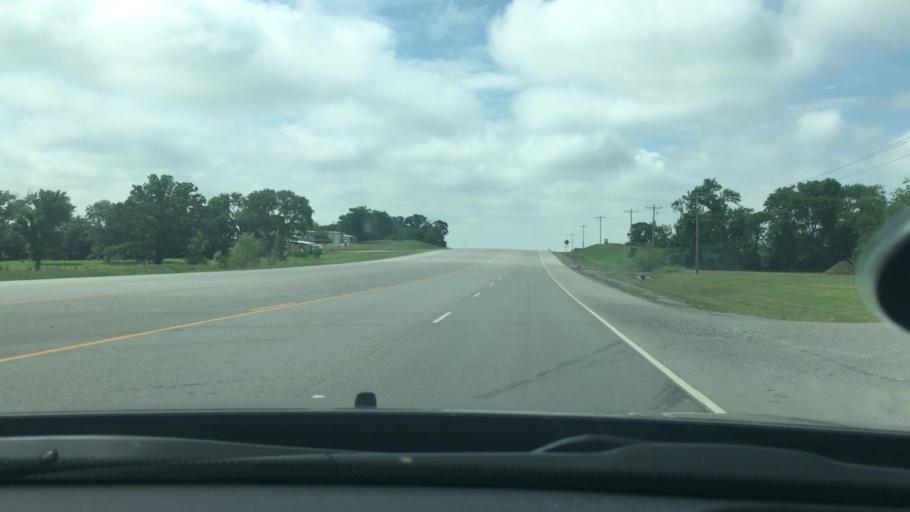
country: US
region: Oklahoma
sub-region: Bryan County
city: Durant
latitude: 34.0591
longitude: -96.3728
